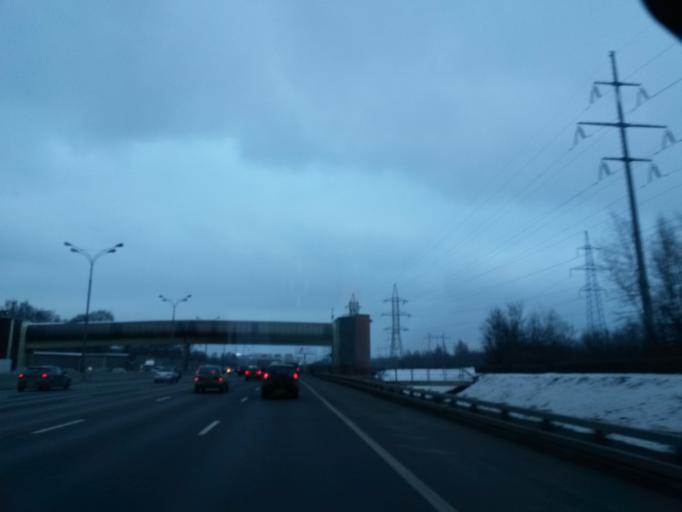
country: RU
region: Moscow
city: Mikhalkovo
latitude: 55.6739
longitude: 37.4238
